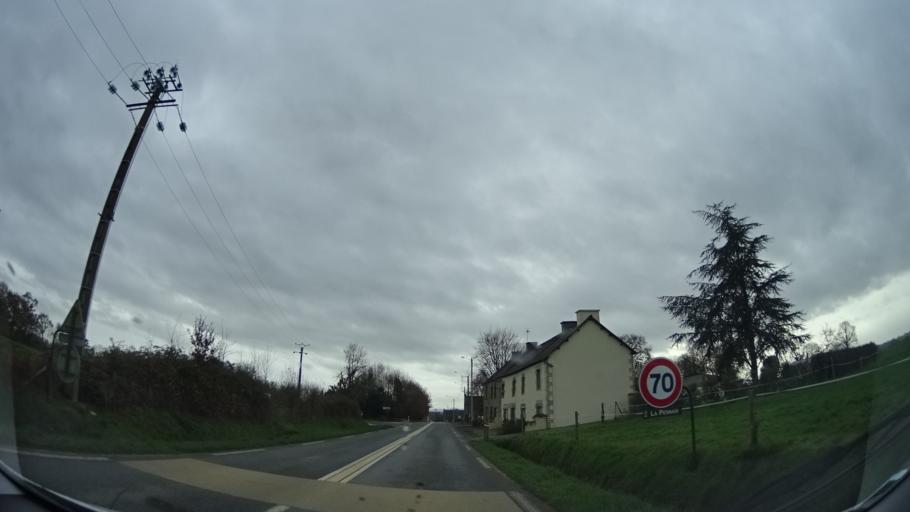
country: FR
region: Brittany
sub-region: Departement des Cotes-d'Armor
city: Dinan
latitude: 48.4266
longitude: -2.0064
